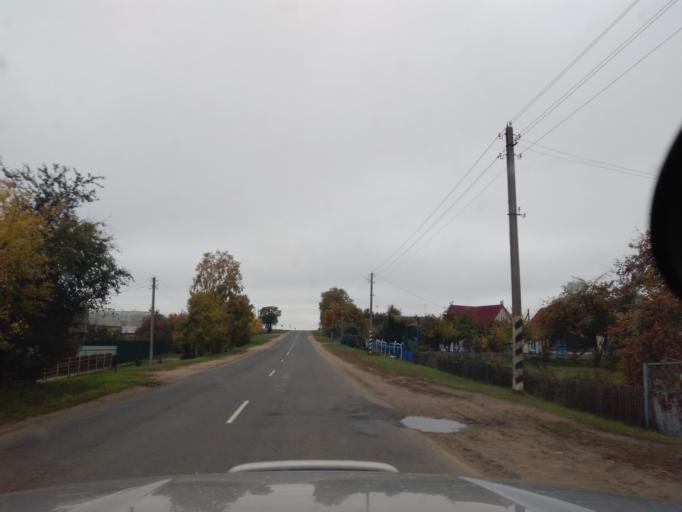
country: BY
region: Minsk
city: Kapyl'
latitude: 53.1504
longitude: 27.1369
